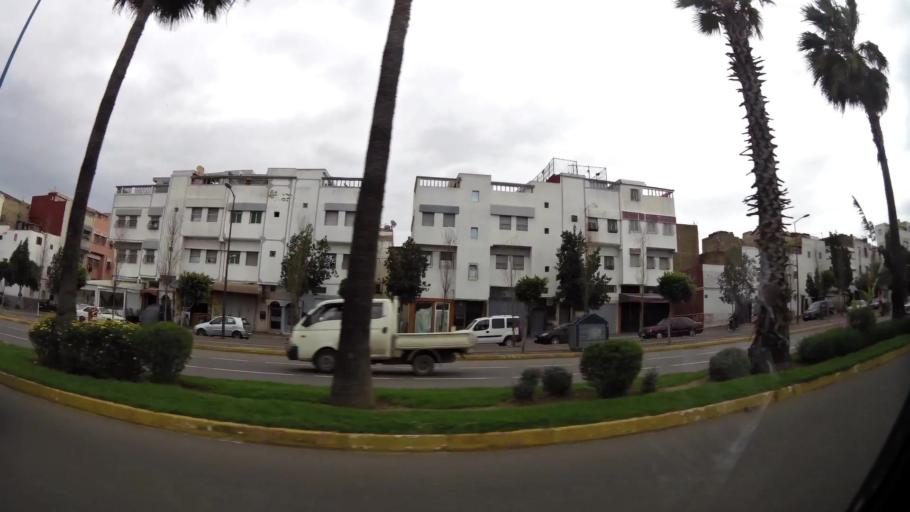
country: MA
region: Grand Casablanca
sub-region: Casablanca
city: Casablanca
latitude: 33.5538
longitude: -7.5550
